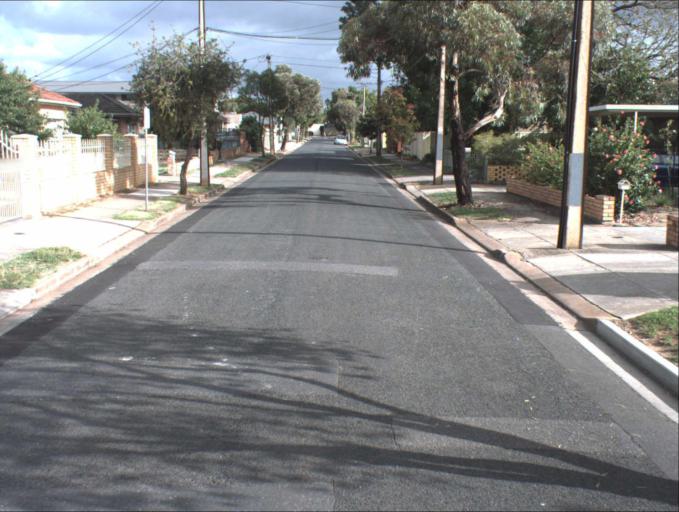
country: AU
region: South Australia
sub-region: Port Adelaide Enfield
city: Klemzig
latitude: -34.8805
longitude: 138.6371
